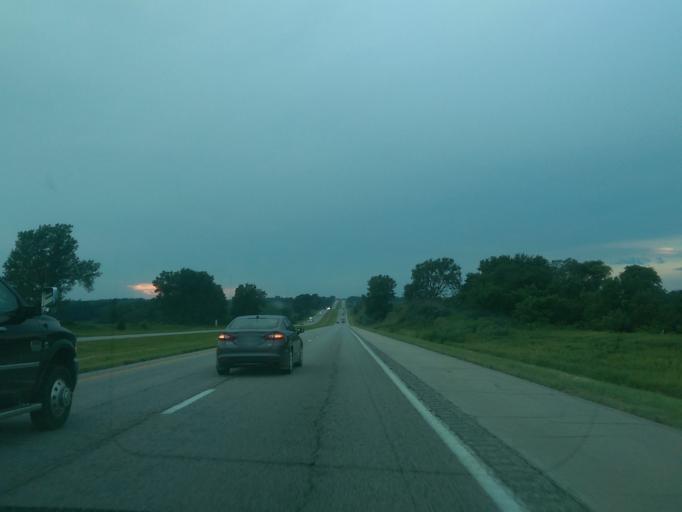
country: US
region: Missouri
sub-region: Holt County
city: Oregon
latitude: 40.0567
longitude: -95.1596
